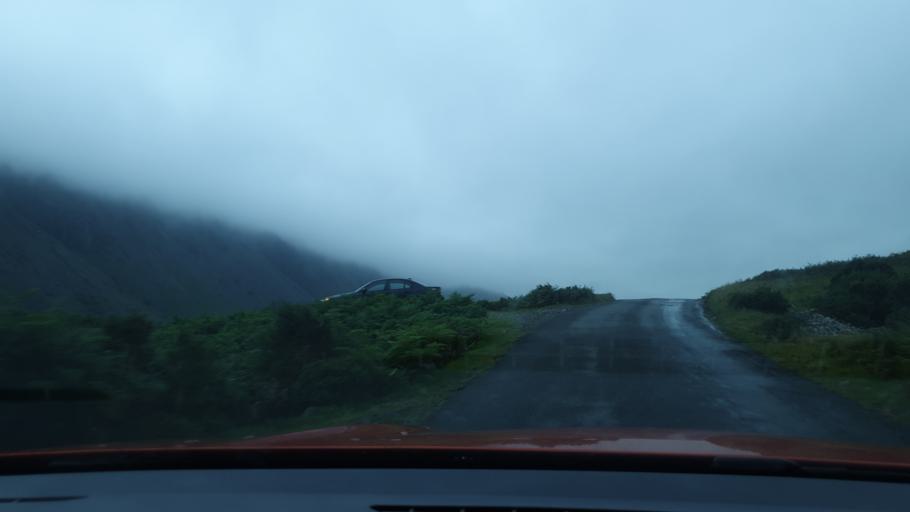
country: GB
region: England
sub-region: Cumbria
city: Seascale
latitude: 54.4435
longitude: -3.3008
